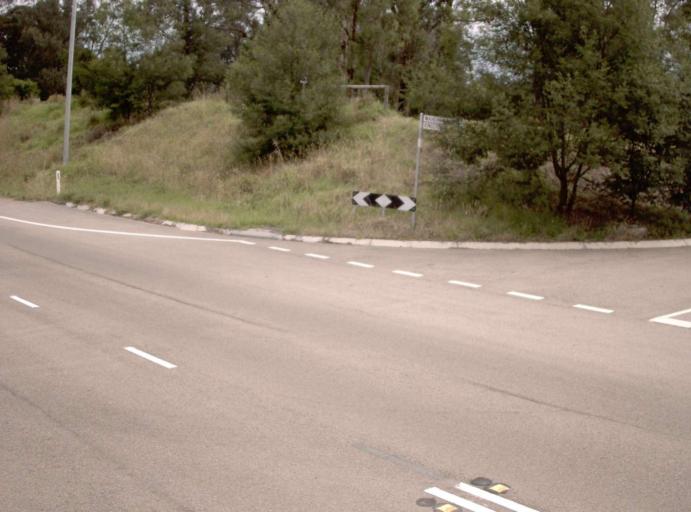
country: AU
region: Victoria
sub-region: East Gippsland
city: Lakes Entrance
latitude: -37.7301
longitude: 148.0895
